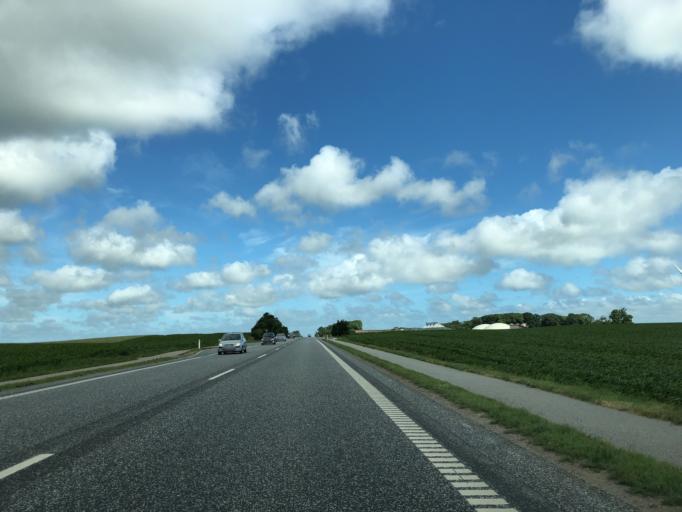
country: DK
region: Central Jutland
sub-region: Holstebro Kommune
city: Holstebro
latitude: 56.4216
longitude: 8.6008
